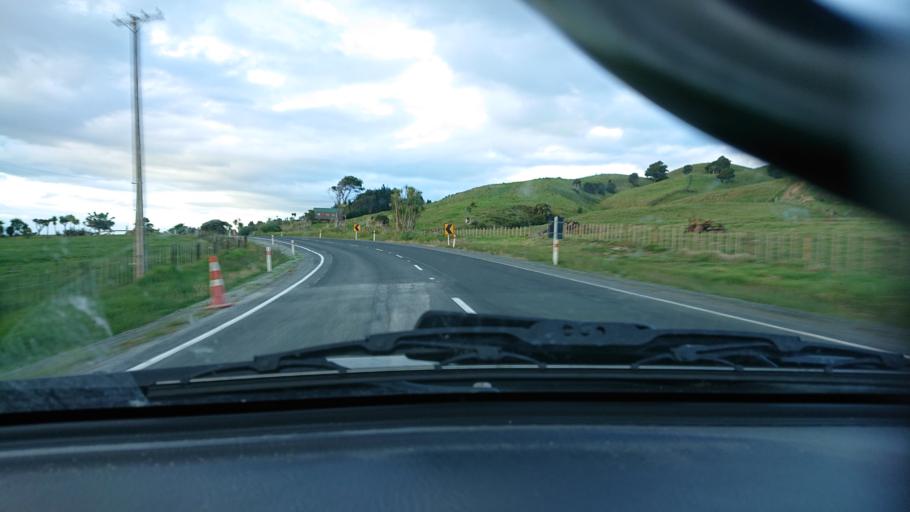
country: NZ
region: Auckland
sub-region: Auckland
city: Wellsford
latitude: -36.4481
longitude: 174.4336
